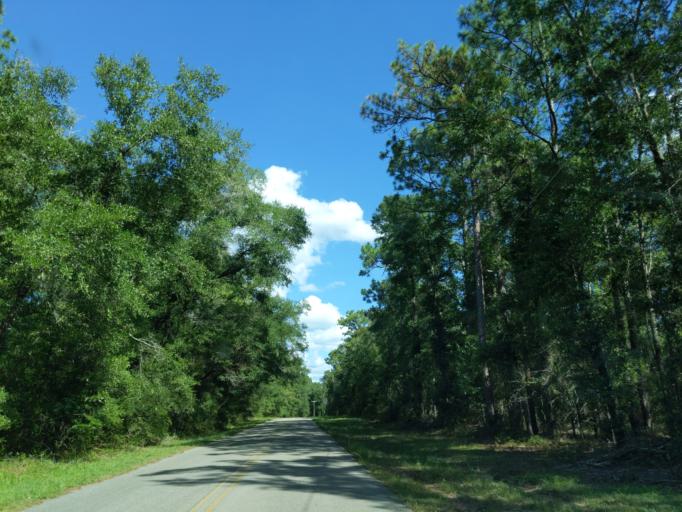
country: US
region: Florida
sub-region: Leon County
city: Tallahassee
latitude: 30.4025
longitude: -84.3444
